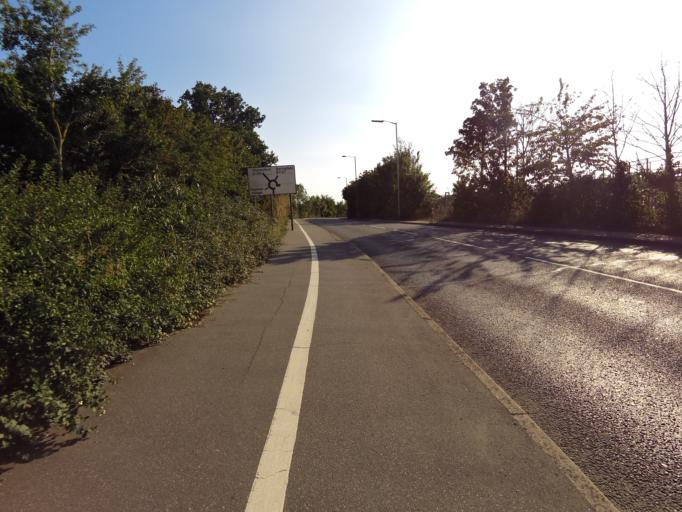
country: GB
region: England
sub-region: Essex
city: Chelmsford
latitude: 51.7482
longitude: 0.5075
